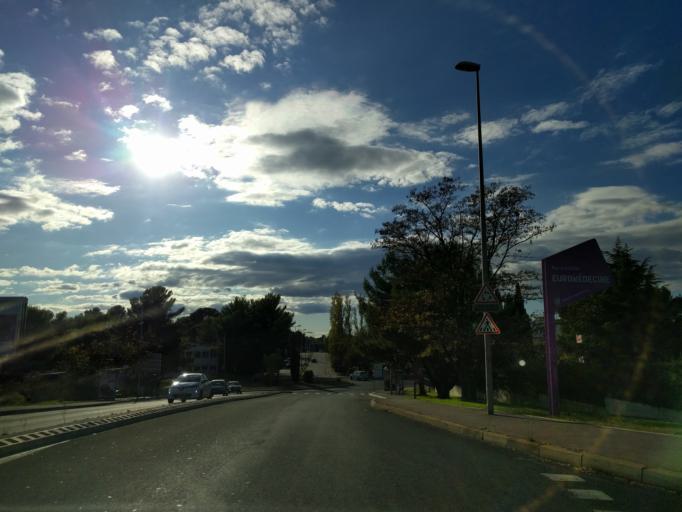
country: FR
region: Languedoc-Roussillon
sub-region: Departement de l'Herault
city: Montferrier-sur-Lez
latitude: 43.6450
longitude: 3.8426
